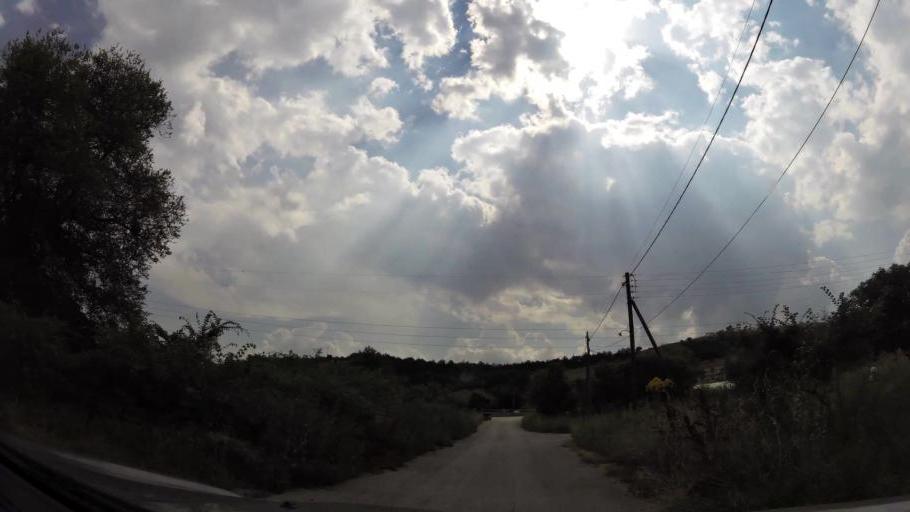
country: GR
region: West Macedonia
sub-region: Nomos Kozanis
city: Koila
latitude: 40.3475
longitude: 21.8238
